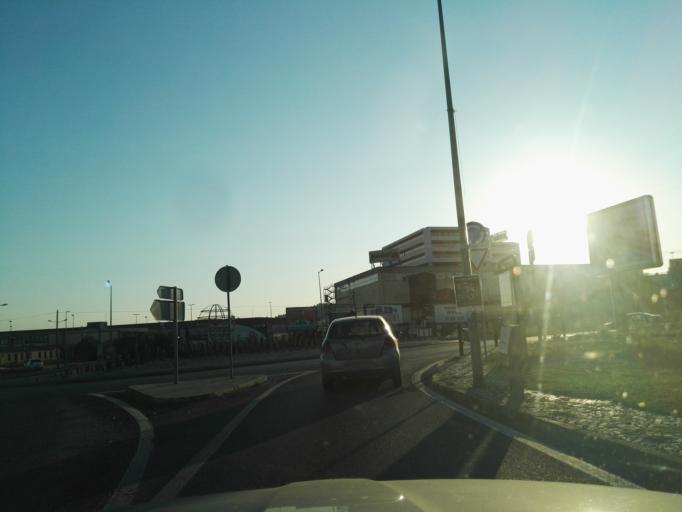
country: PT
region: Lisbon
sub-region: Vila Franca de Xira
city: Sobralinho
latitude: 38.8894
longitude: -9.0411
